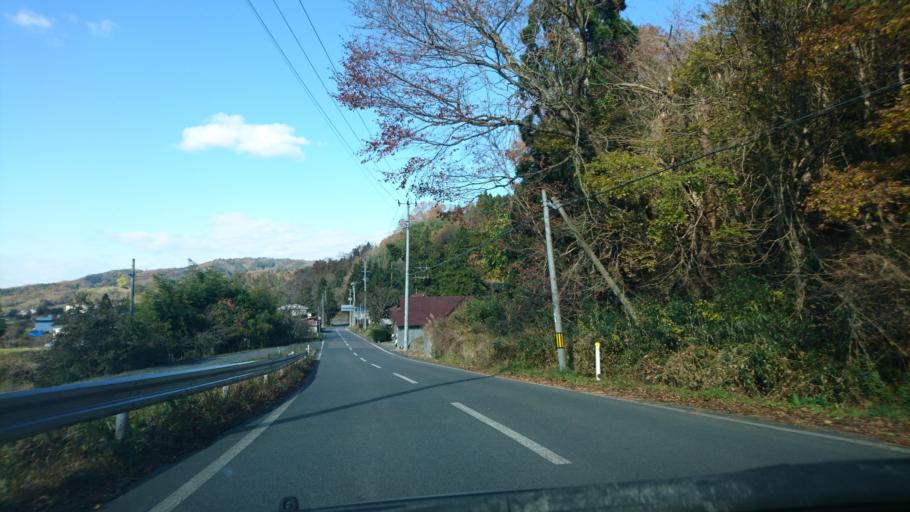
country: JP
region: Iwate
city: Ichinoseki
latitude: 39.0138
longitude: 141.4109
